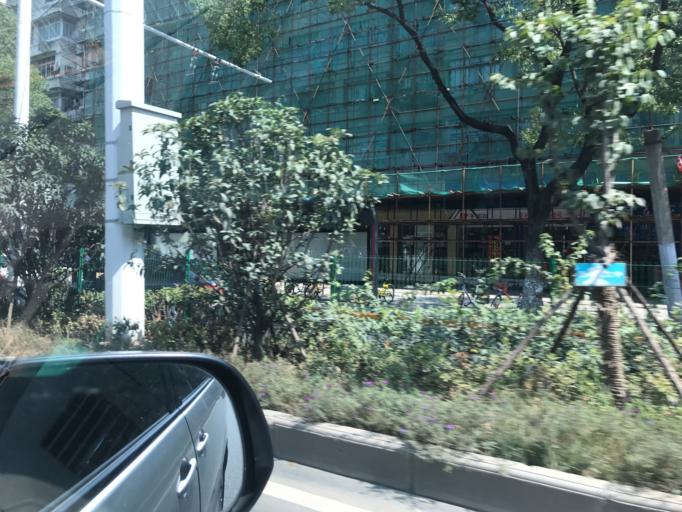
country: CN
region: Hubei
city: Yongfeng
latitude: 30.5602
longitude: 114.2203
